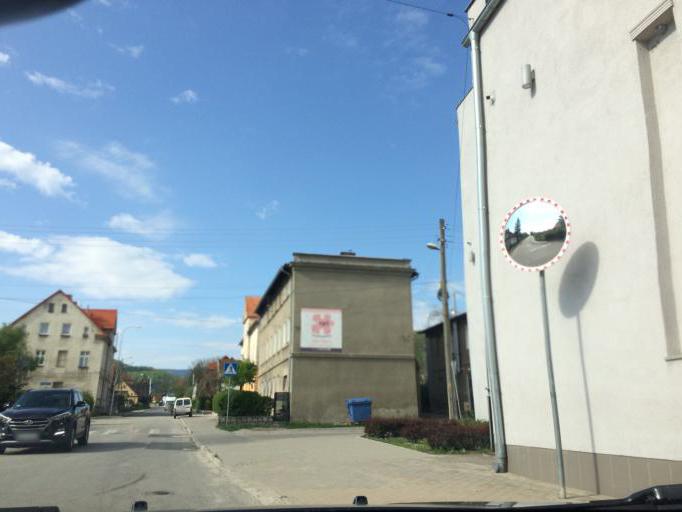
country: PL
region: Lower Silesian Voivodeship
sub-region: Powiat dzierzoniowski
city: Pieszyce
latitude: 50.7079
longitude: 16.5755
